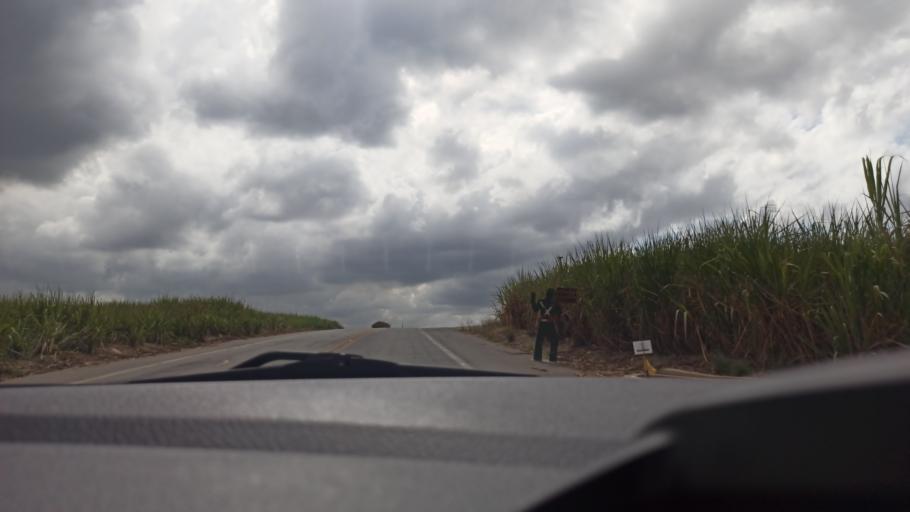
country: BR
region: Pernambuco
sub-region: Timbauba
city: Timbauba
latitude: -7.5450
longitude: -35.2696
